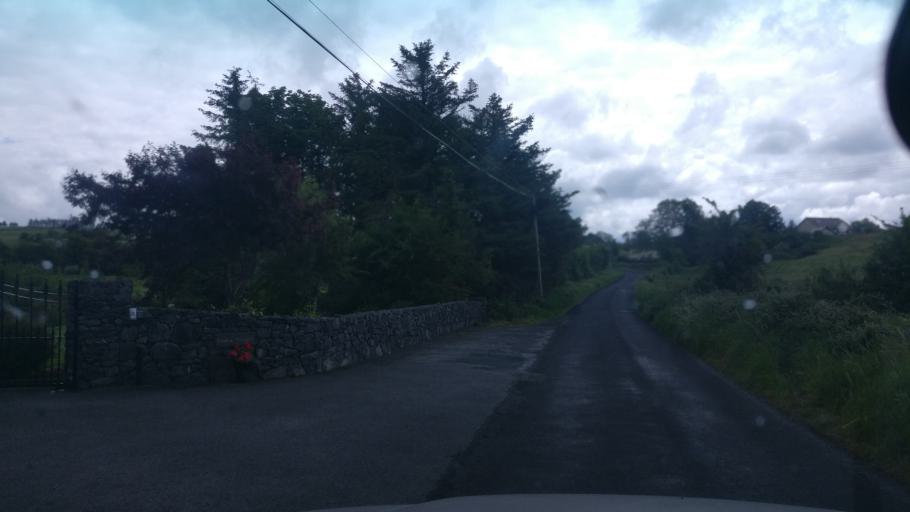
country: IE
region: Connaught
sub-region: County Galway
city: Loughrea
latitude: 53.1693
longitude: -8.5698
